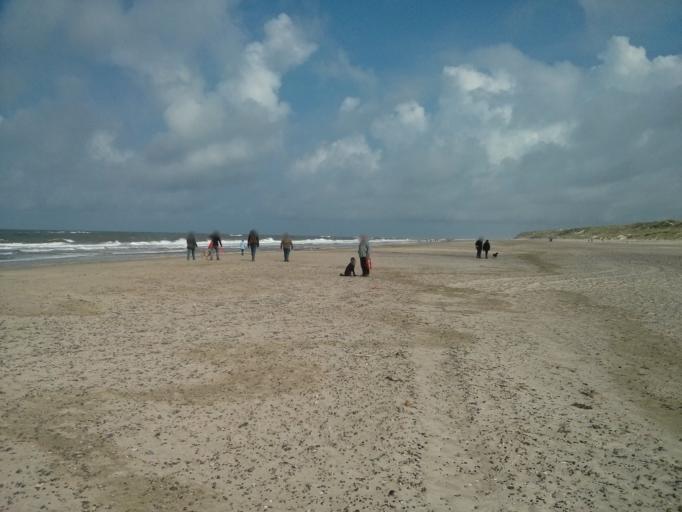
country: DK
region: Central Jutland
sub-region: Ringkobing-Skjern Kommune
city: Hvide Sande
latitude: 55.8632
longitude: 8.1584
